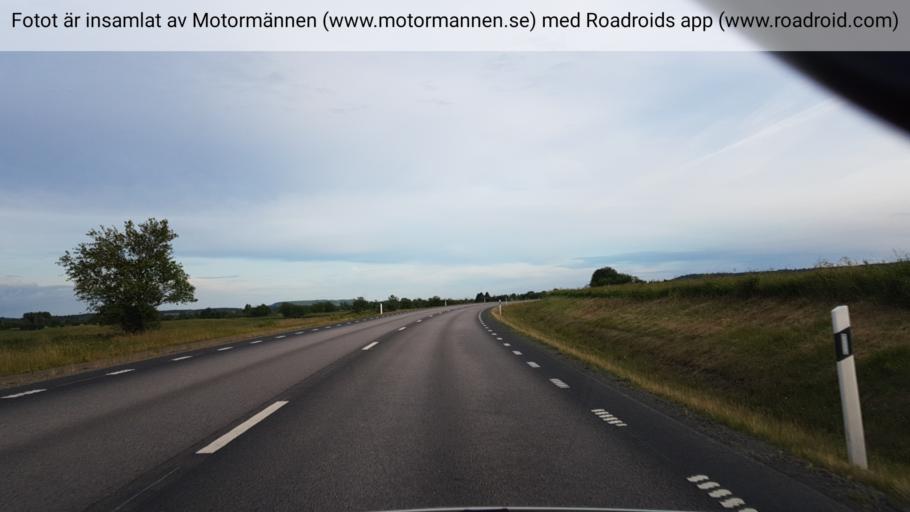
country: SE
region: Vaestra Goetaland
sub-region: Falkopings Kommun
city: Falkoeping
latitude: 58.2228
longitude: 13.5660
